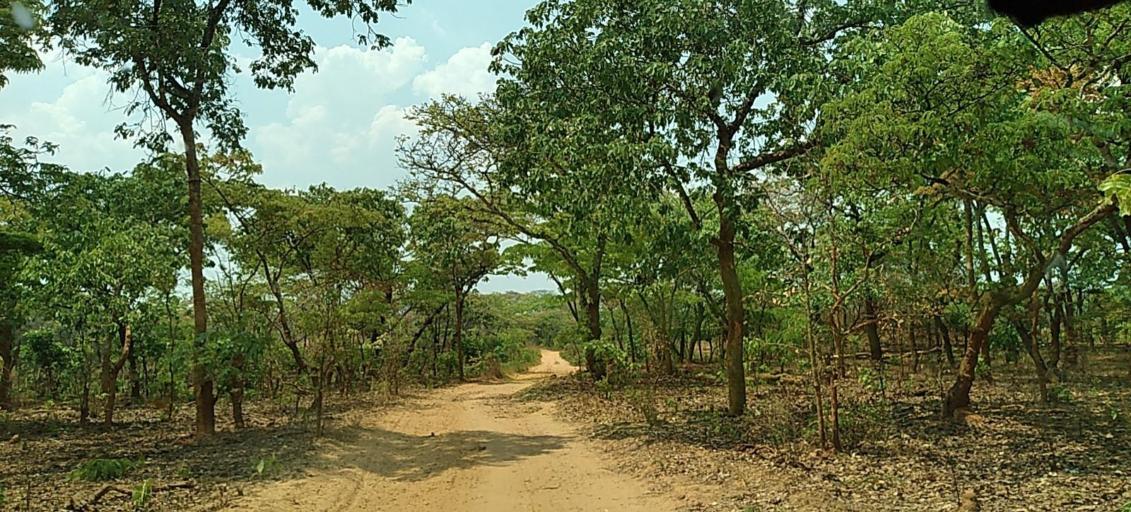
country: ZM
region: North-Western
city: Kabompo
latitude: -13.6474
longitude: 24.3766
